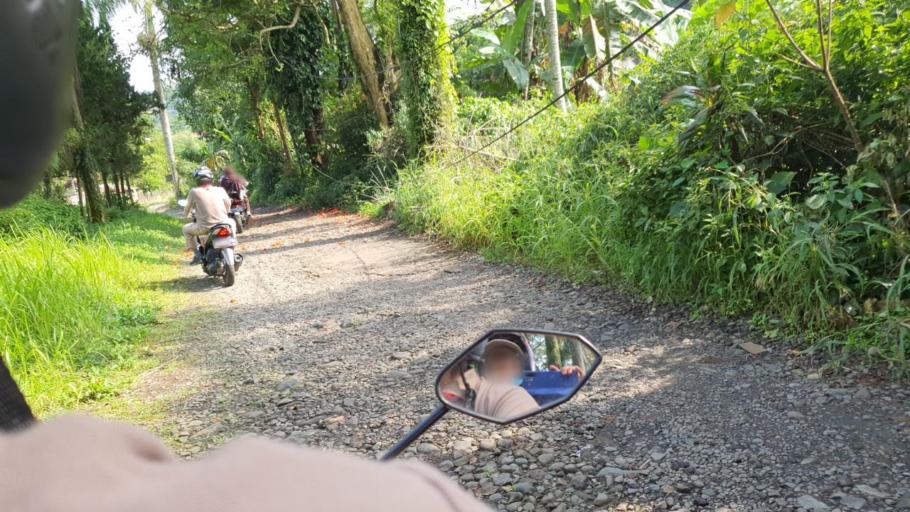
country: ID
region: West Java
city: Caringin
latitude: -6.6546
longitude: 106.8711
